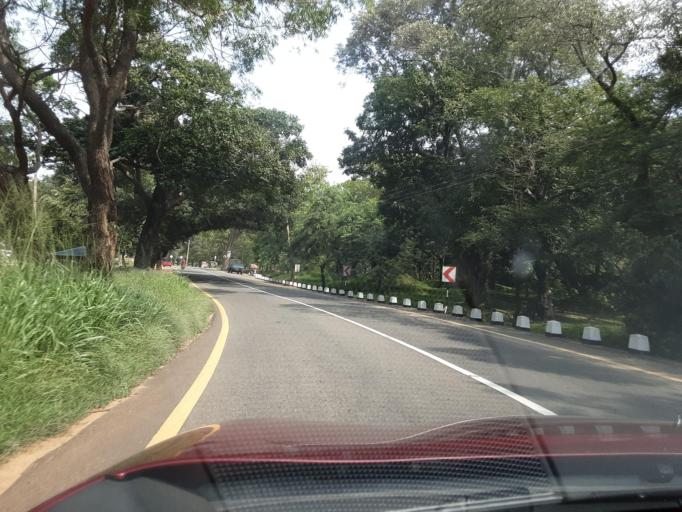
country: LK
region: North Central
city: Anuradhapura
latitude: 8.3515
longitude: 80.5093
